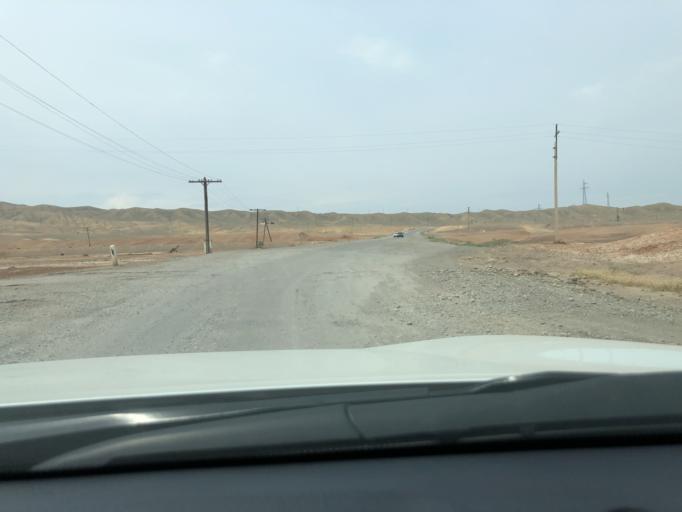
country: TJ
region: Viloyati Sughd
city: Kim
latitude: 40.2095
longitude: 70.4749
